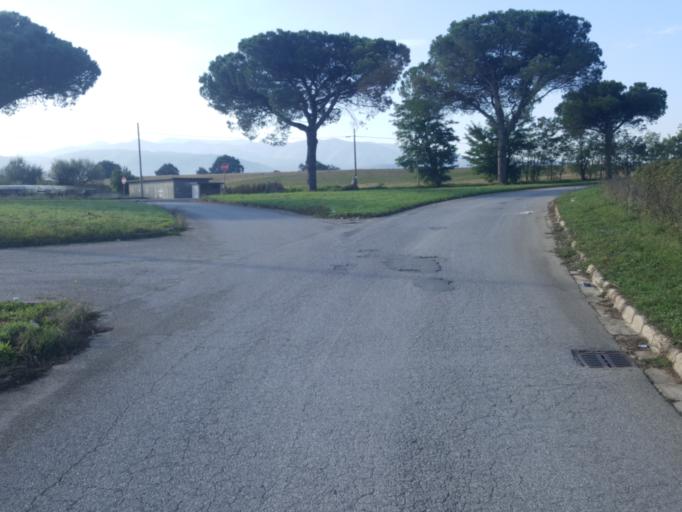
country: IT
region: Latium
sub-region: Citta metropolitana di Roma Capitale
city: Colleferro
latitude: 41.7561
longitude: 13.0017
